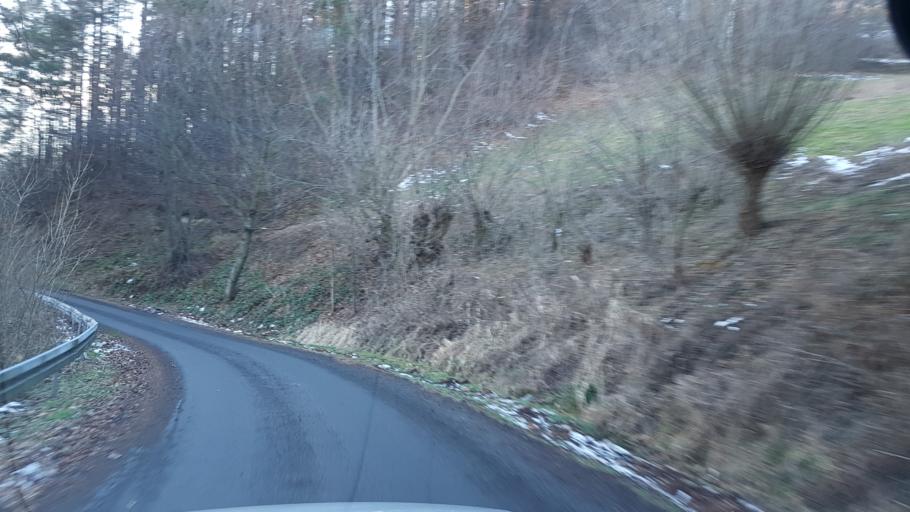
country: PL
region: Lesser Poland Voivodeship
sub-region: Powiat nowosadecki
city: Rytro
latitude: 49.4919
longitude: 20.6684
